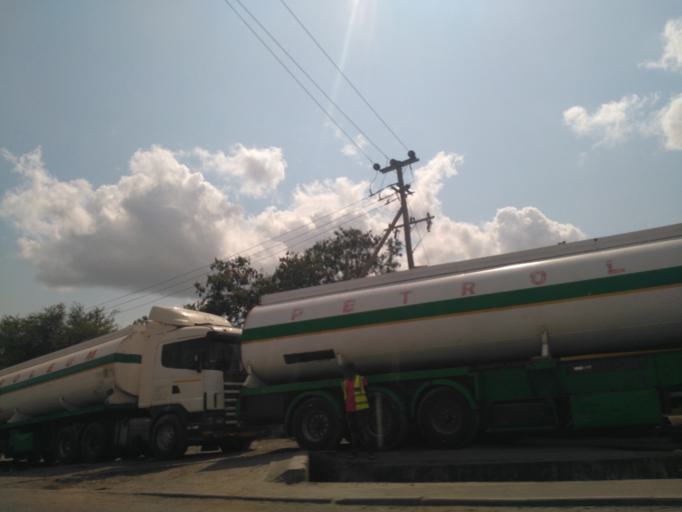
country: TZ
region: Dar es Salaam
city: Dar es Salaam
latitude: -6.8429
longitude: 39.2937
